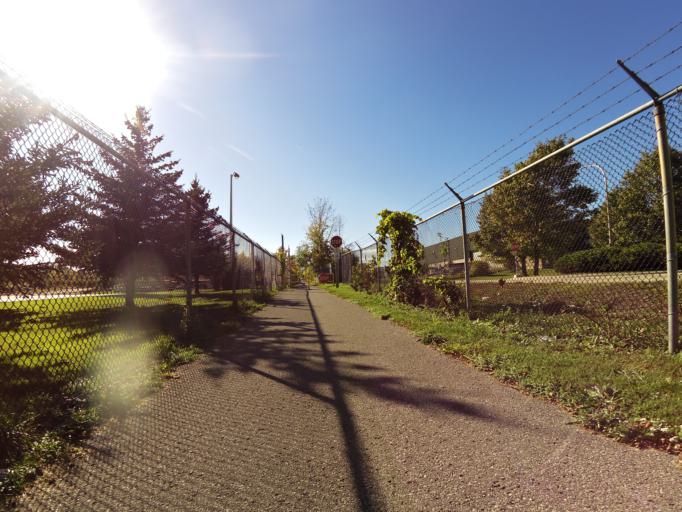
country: CA
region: Ontario
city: Oshawa
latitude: 43.8577
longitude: -78.8928
